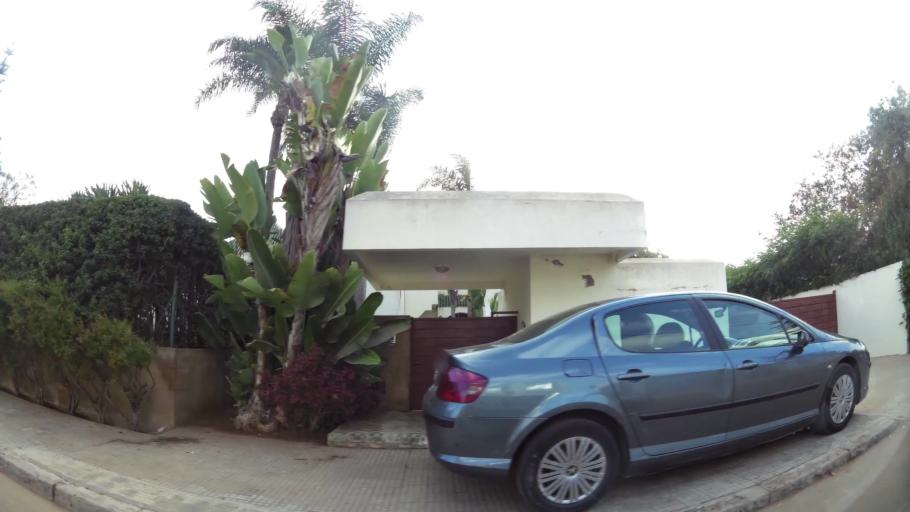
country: MA
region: Rabat-Sale-Zemmour-Zaer
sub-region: Rabat
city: Rabat
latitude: 33.9571
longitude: -6.8390
